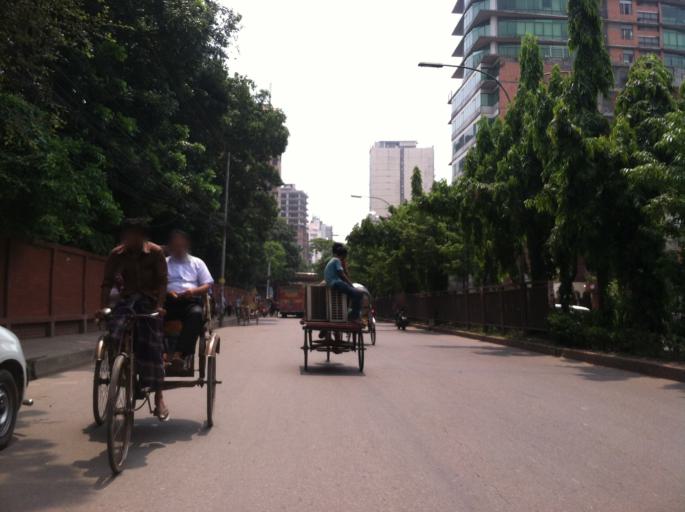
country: BD
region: Dhaka
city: Paltan
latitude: 23.7808
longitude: 90.4030
